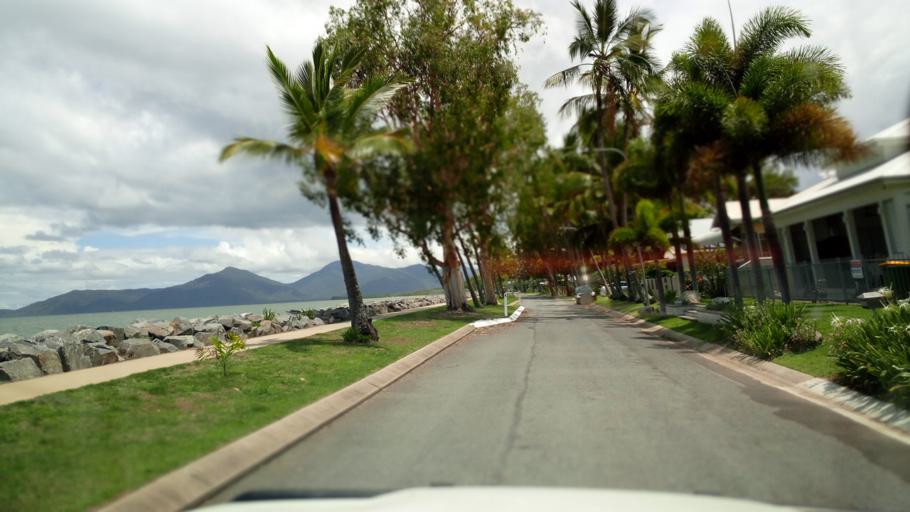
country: AU
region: Queensland
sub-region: Cairns
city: Yorkeys Knob
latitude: -16.8474
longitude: 145.7467
